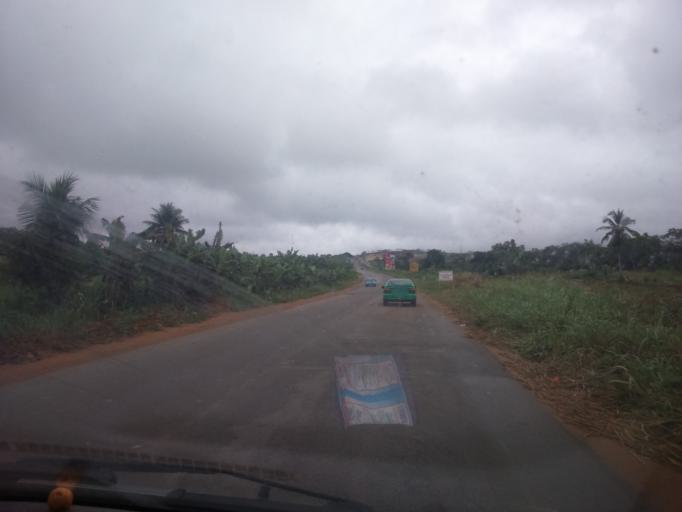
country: CI
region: Sud-Comoe
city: Bonoua
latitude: 5.2491
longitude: -3.6197
